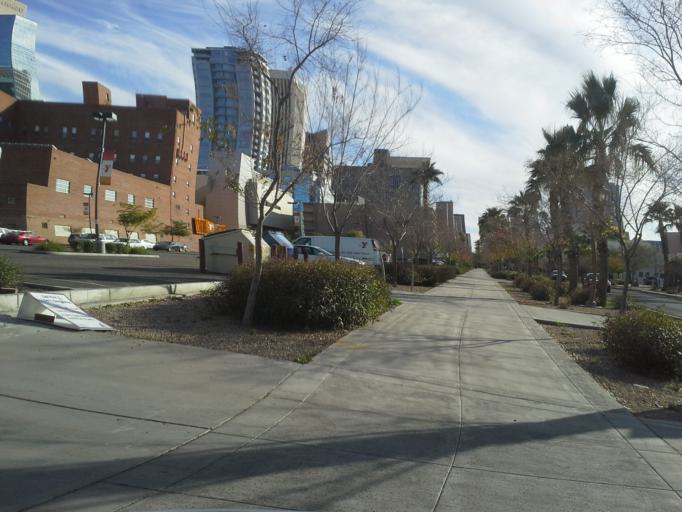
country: US
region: Arizona
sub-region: Maricopa County
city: Phoenix
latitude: 33.4541
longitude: -112.0763
